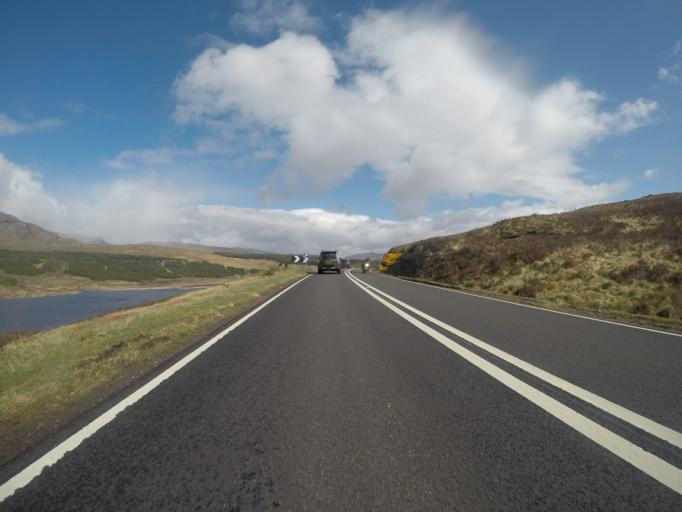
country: GB
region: Scotland
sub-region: Highland
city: Spean Bridge
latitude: 57.1146
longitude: -4.9834
